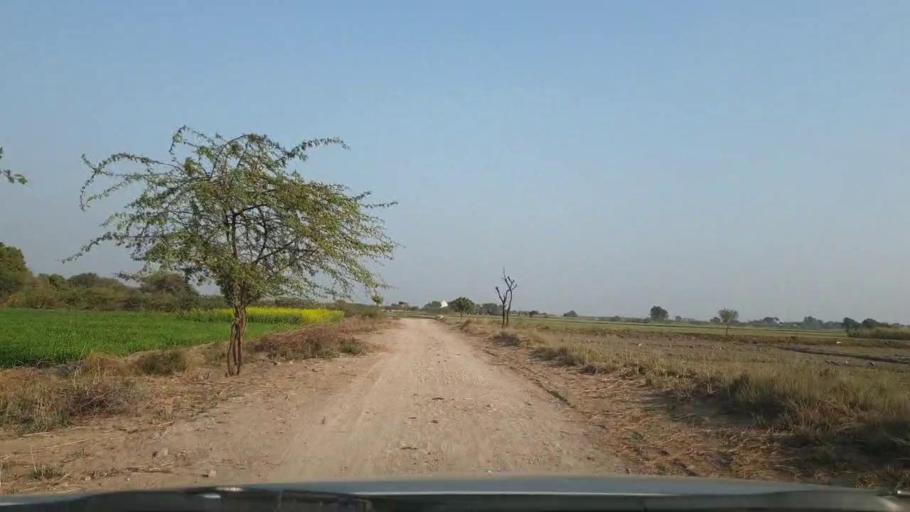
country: PK
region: Sindh
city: Tando Adam
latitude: 25.6707
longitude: 68.6424
